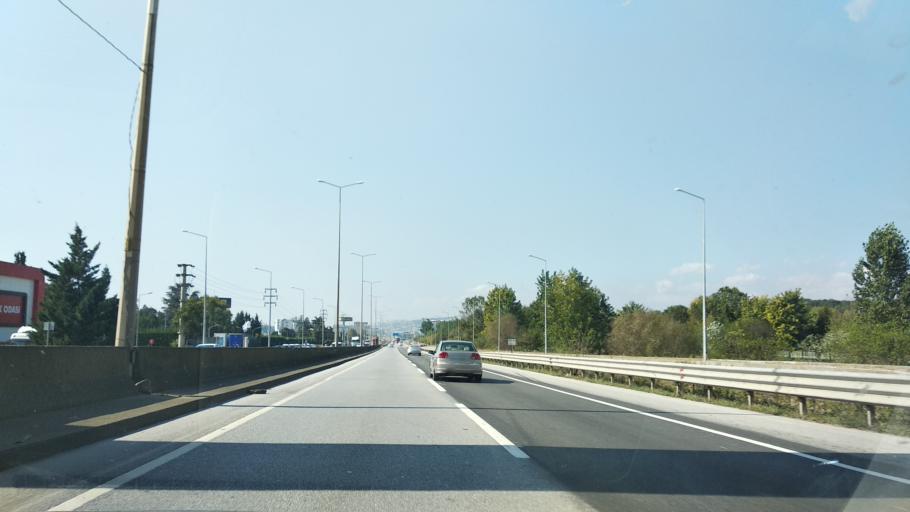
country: TR
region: Kocaeli
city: Kosekoy
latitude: 40.7562
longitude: 30.0037
